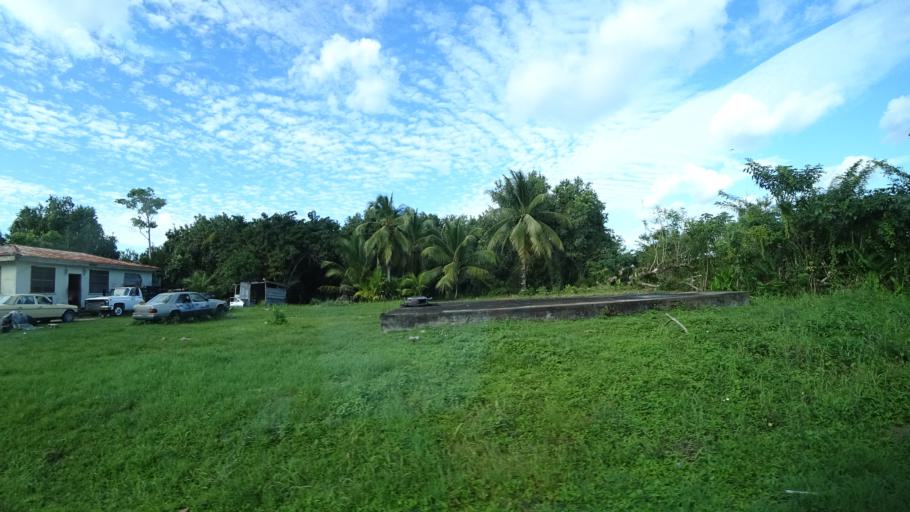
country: BZ
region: Belize
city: Belize City
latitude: 17.5655
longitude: -88.4075
